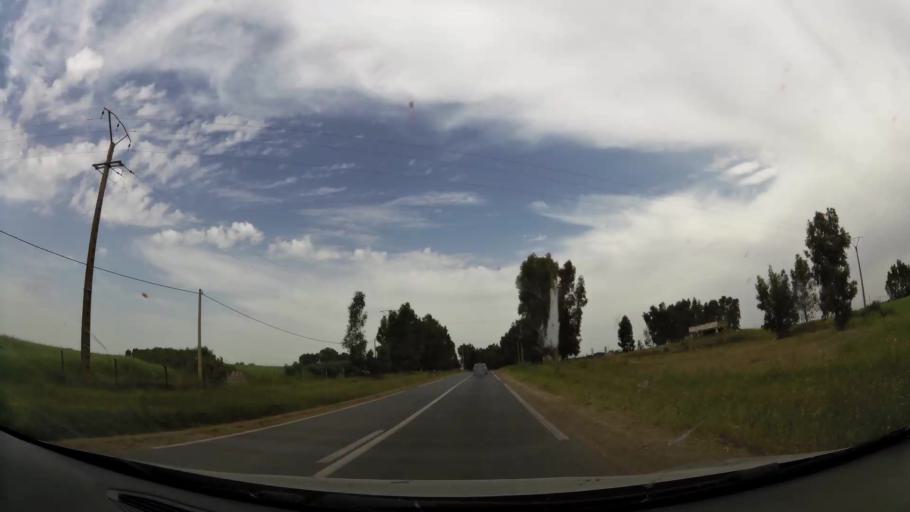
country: MA
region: Rabat-Sale-Zemmour-Zaer
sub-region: Khemisset
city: Tiflet
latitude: 33.8715
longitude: -6.2778
